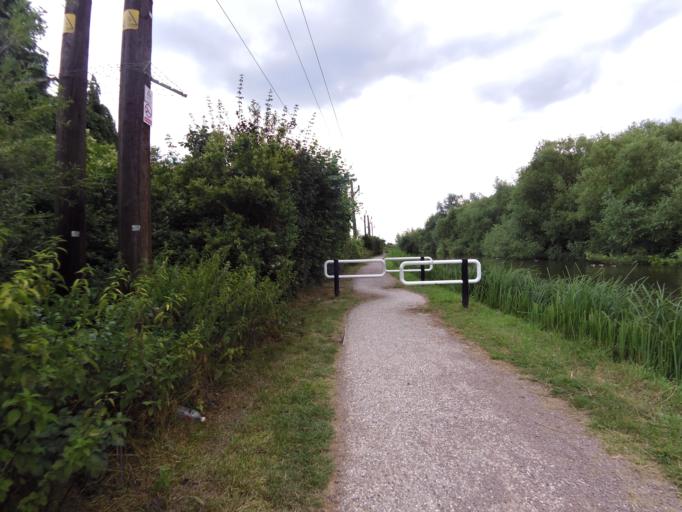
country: GB
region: England
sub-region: Hertfordshire
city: Broxbourne
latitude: 51.7320
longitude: -0.0140
